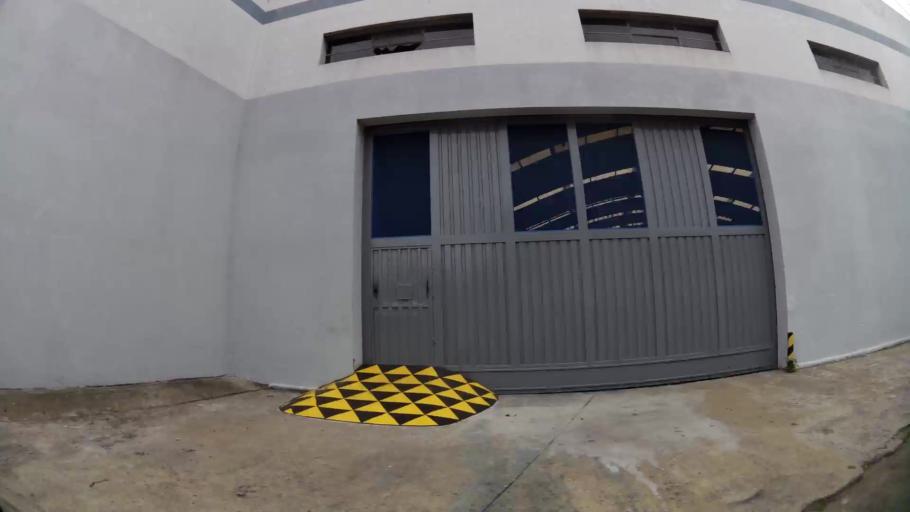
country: AR
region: Buenos Aires
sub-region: Partido de Avellaneda
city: Avellaneda
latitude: -34.6800
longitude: -58.3824
